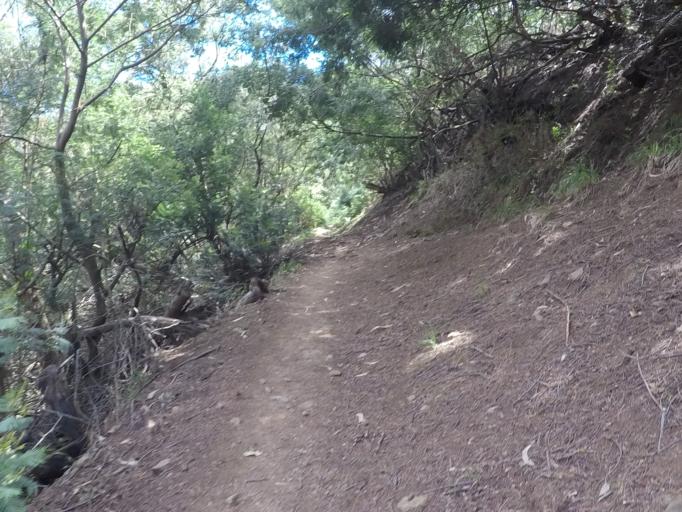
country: PT
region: Madeira
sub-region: Machico
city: Canical
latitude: 32.7499
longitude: -16.7718
